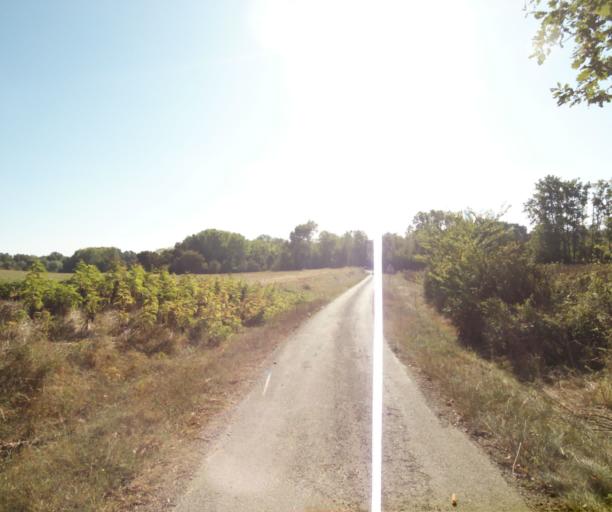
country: FR
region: Midi-Pyrenees
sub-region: Departement du Tarn-et-Garonne
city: Verdun-sur-Garonne
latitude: 43.8648
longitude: 1.2199
